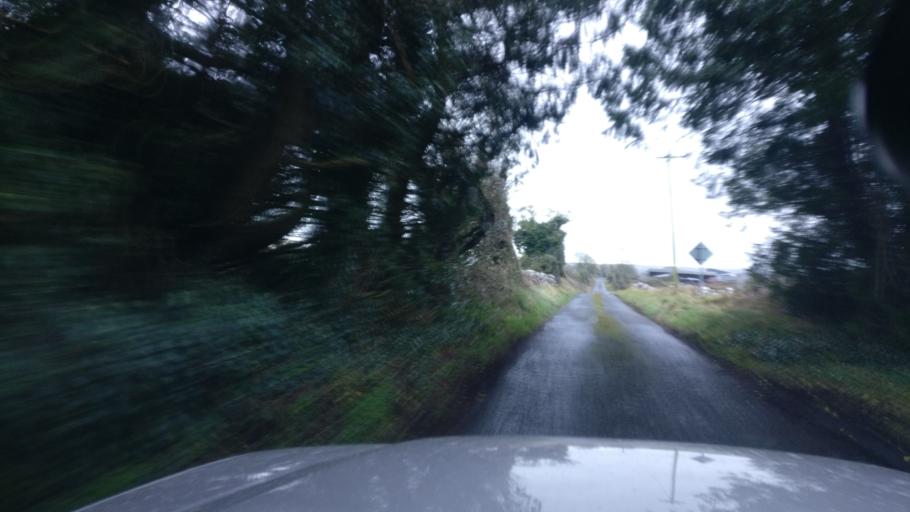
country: IE
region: Connaught
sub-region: County Galway
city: Loughrea
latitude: 53.2054
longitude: -8.6490
